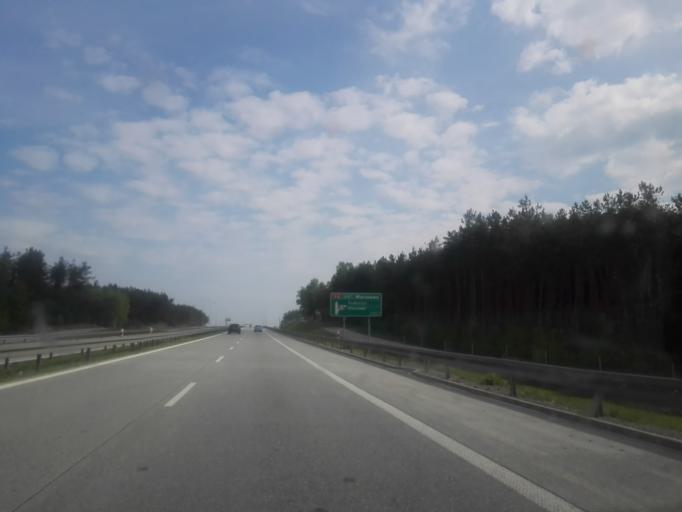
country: PL
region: Lodz Voivodeship
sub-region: Powiat tomaszowski
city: Czerniewice
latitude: 51.6975
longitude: 20.2163
